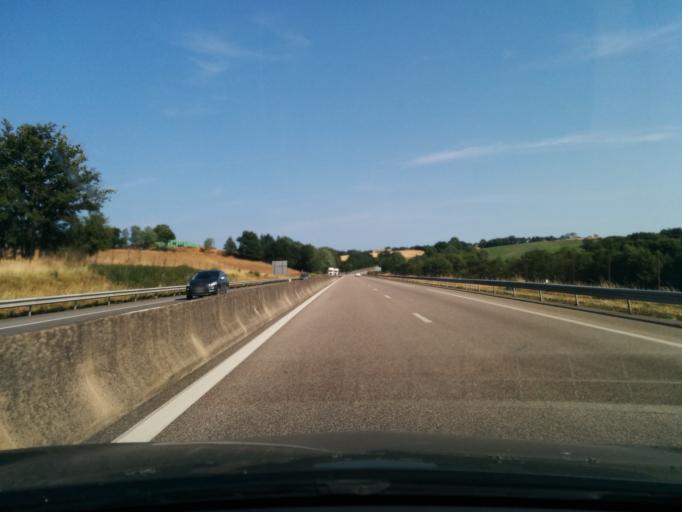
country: FR
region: Limousin
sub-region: Departement de la Haute-Vienne
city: Pierre-Buffiere
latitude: 45.7265
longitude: 1.3438
